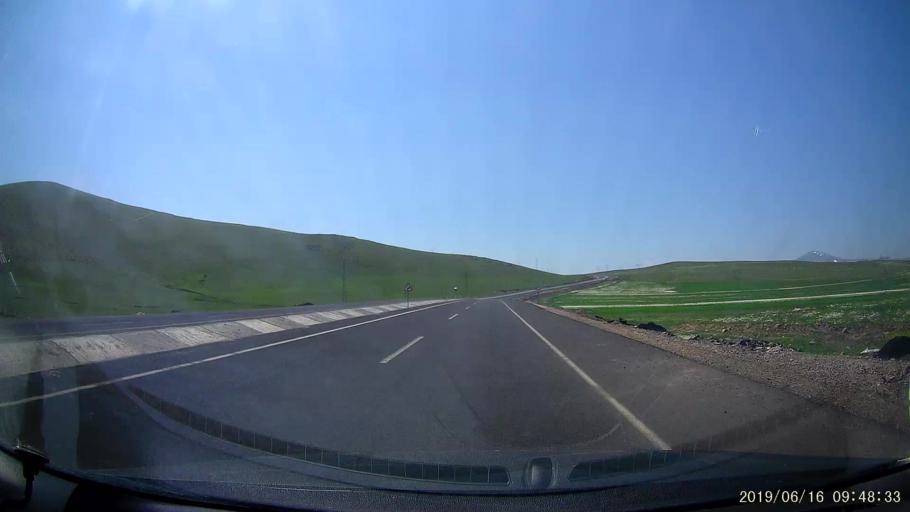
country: TR
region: Kars
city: Digor
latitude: 40.4324
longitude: 43.3539
